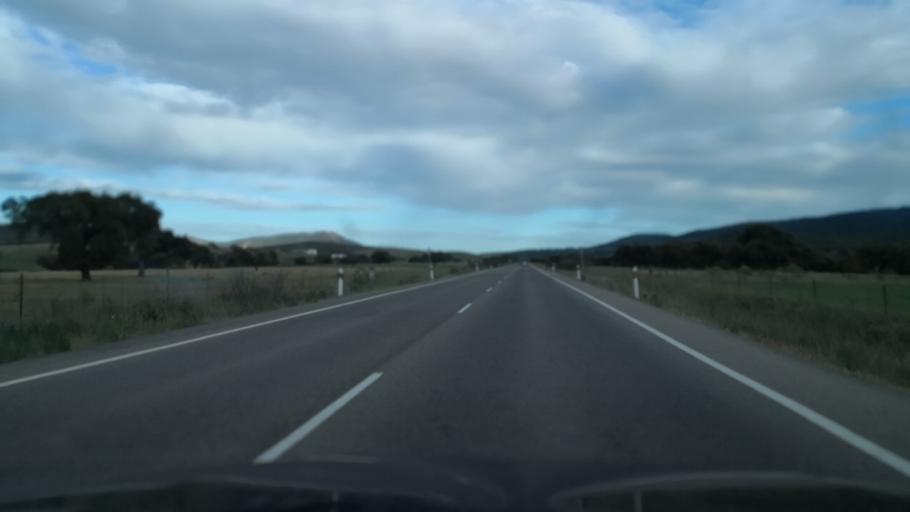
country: ES
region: Extremadura
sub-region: Provincia de Caceres
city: Pedroso de Acim
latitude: 39.8580
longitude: -6.4257
